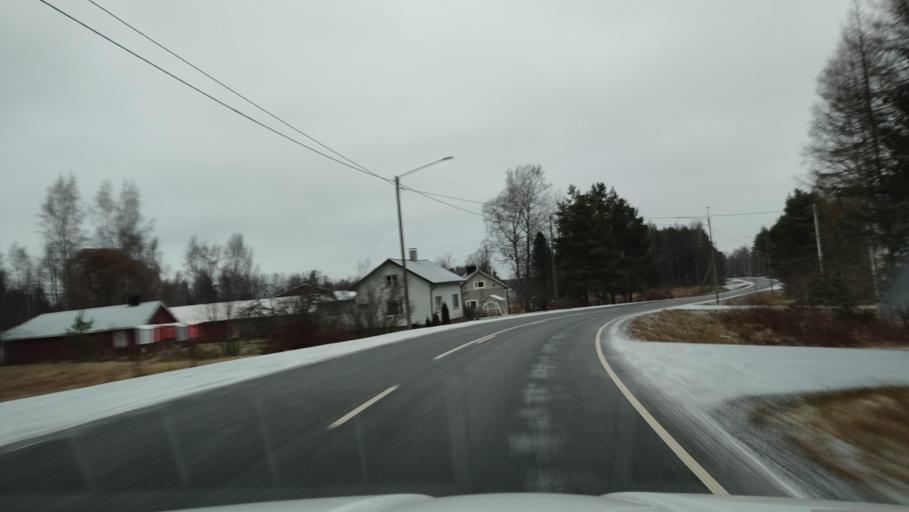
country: FI
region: Southern Ostrobothnia
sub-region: Suupohja
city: Karijoki
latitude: 62.3008
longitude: 21.6840
